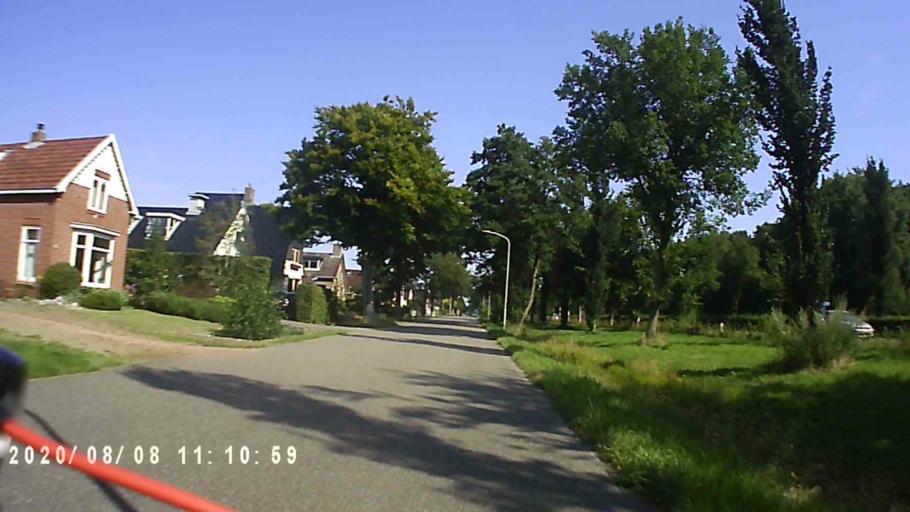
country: NL
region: Groningen
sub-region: Gemeente Leek
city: Leek
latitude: 53.1692
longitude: 6.3810
